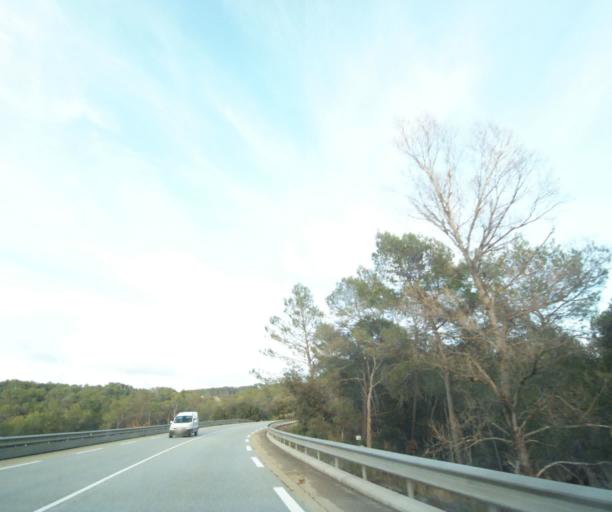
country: FR
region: Provence-Alpes-Cote d'Azur
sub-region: Departement du Var
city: La Motte
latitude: 43.5169
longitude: 6.5175
